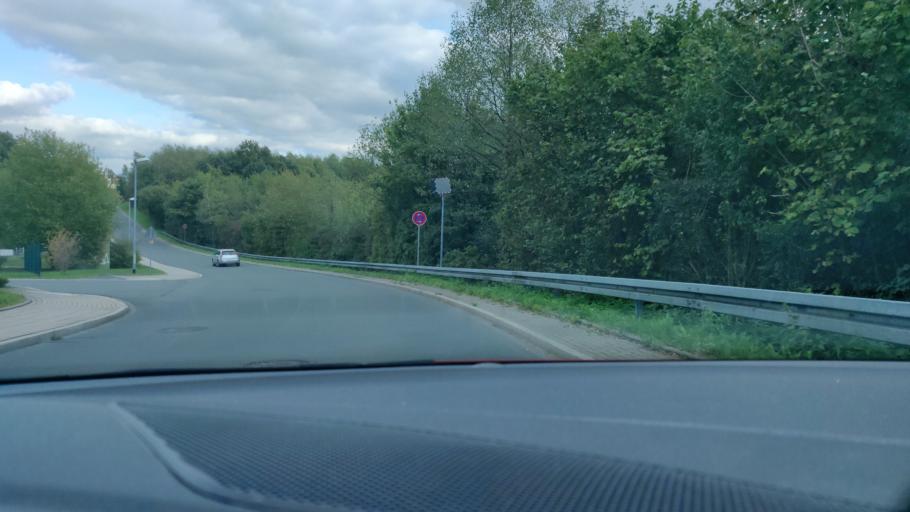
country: DE
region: North Rhine-Westphalia
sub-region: Regierungsbezirk Dusseldorf
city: Velbert
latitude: 51.3269
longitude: 7.0408
